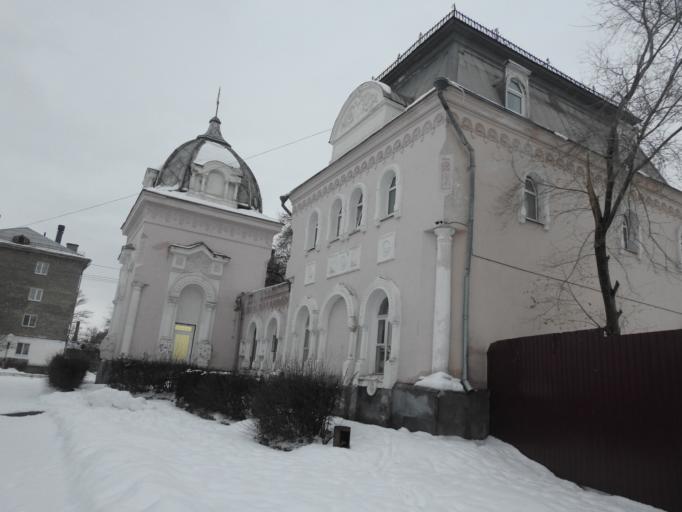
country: RU
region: Saratov
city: Vol'sk
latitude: 52.0400
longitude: 47.3974
